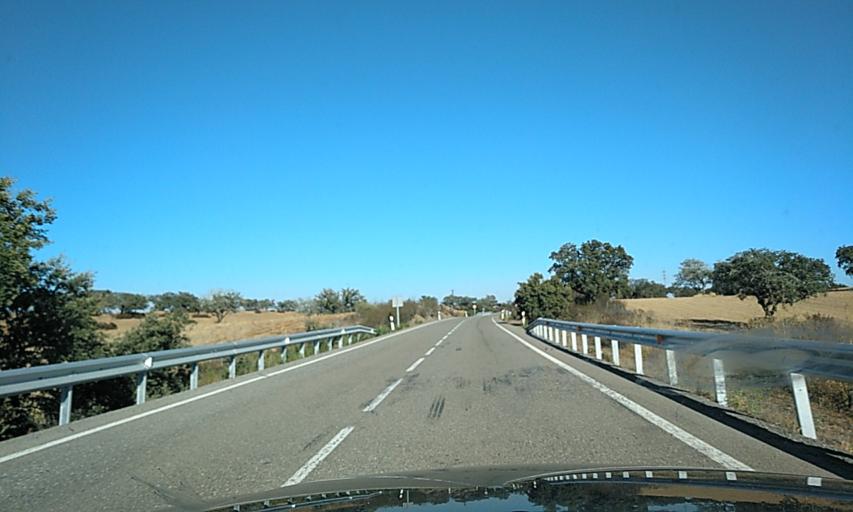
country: ES
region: Andalusia
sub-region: Provincia de Huelva
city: Santa Barbara de Casa
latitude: 37.7810
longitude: -7.1589
